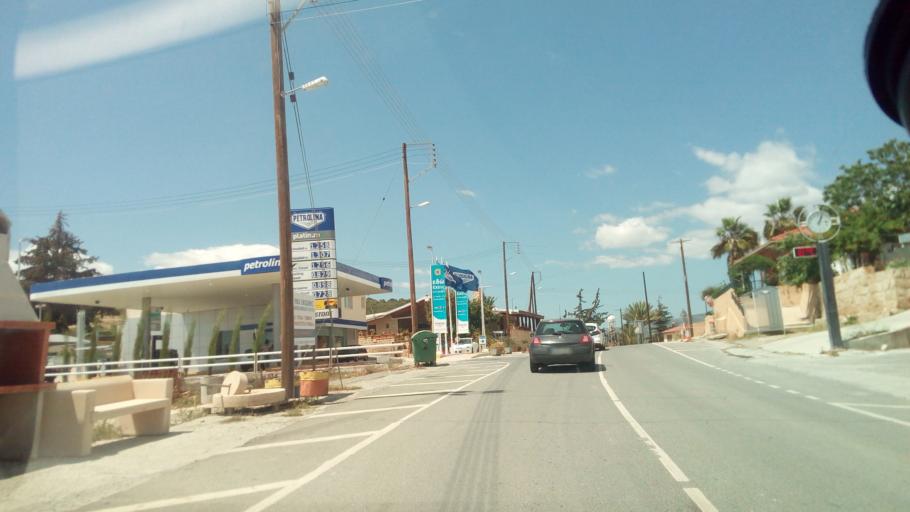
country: CY
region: Limassol
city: Sotira
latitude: 34.7605
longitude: 32.8453
